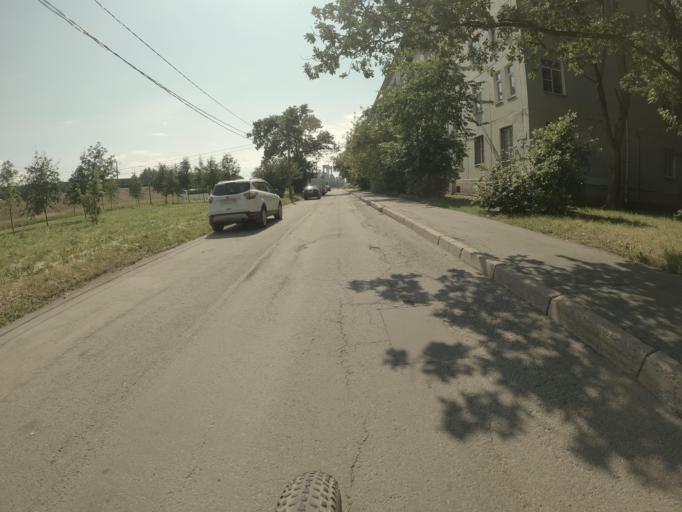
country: RU
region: St.-Petersburg
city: Centralniy
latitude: 59.9189
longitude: 30.4190
